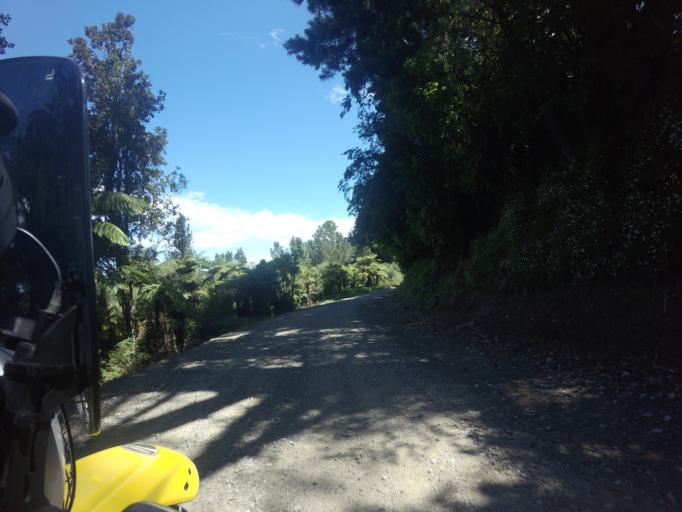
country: NZ
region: Hawke's Bay
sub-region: Wairoa District
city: Wairoa
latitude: -38.9802
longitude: 177.7037
